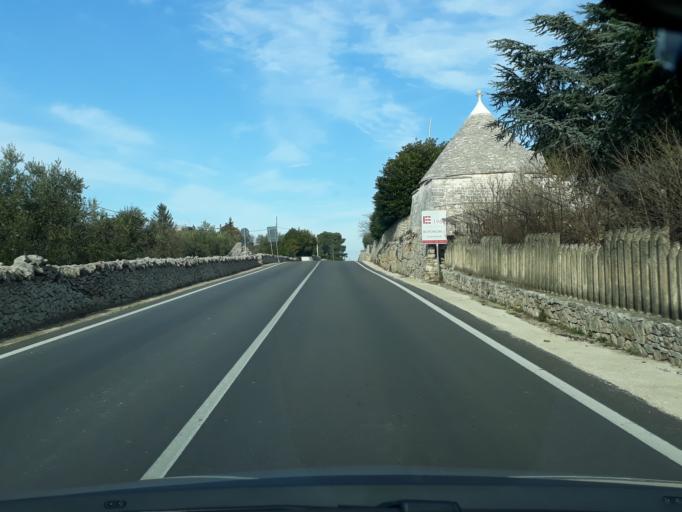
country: IT
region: Apulia
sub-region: Provincia di Bari
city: Locorotondo
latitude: 40.7672
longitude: 17.3330
